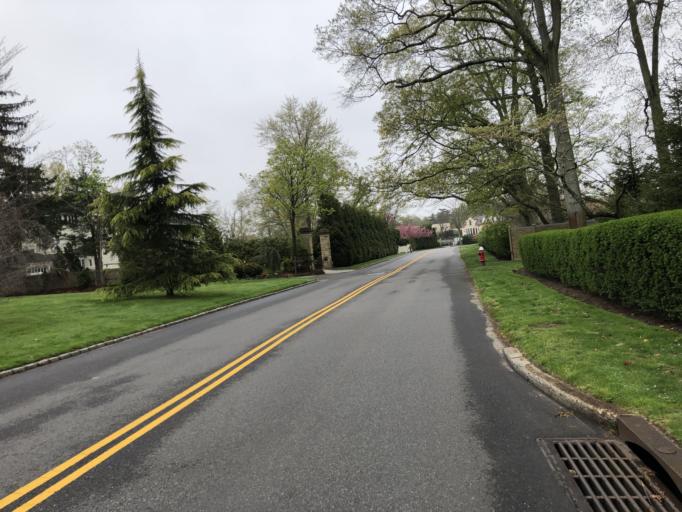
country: US
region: New York
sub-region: Nassau County
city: Hewlett Harbor
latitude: 40.6377
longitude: -73.6891
